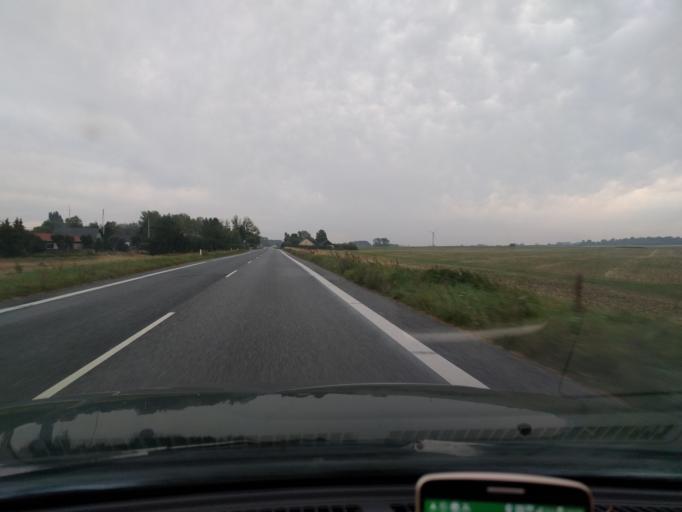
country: DK
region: Zealand
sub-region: Guldborgsund Kommune
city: Norre Alslev
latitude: 54.9380
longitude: 11.8667
